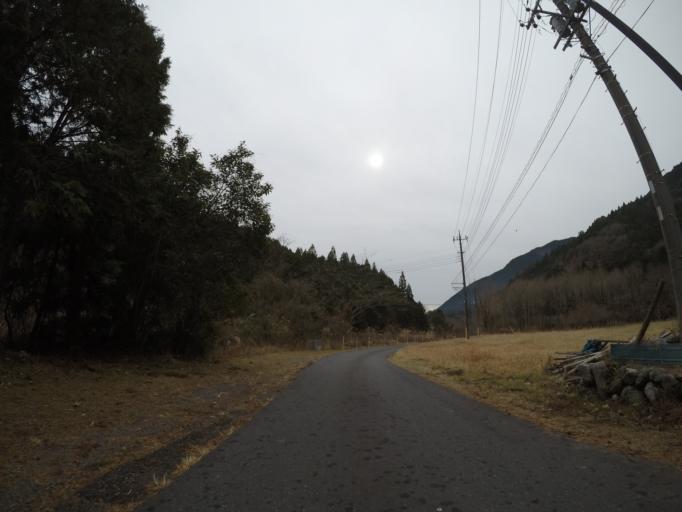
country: JP
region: Shizuoka
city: Fujinomiya
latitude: 35.2712
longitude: 138.5303
